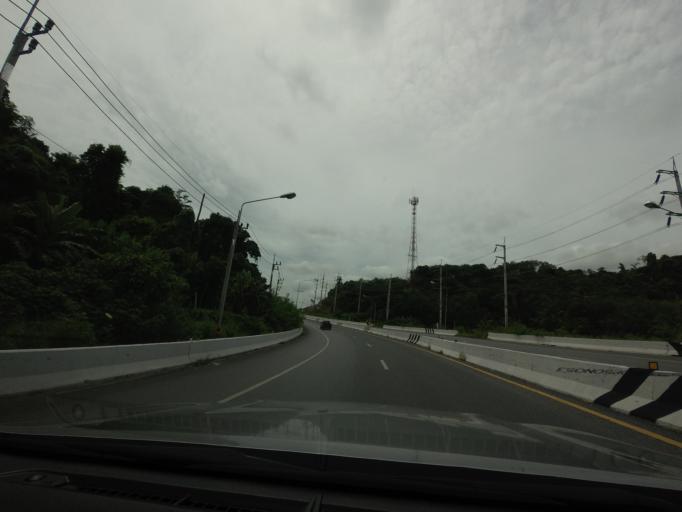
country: TH
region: Nakhon Si Thammarat
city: Hua Sai
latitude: 8.0613
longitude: 100.2009
